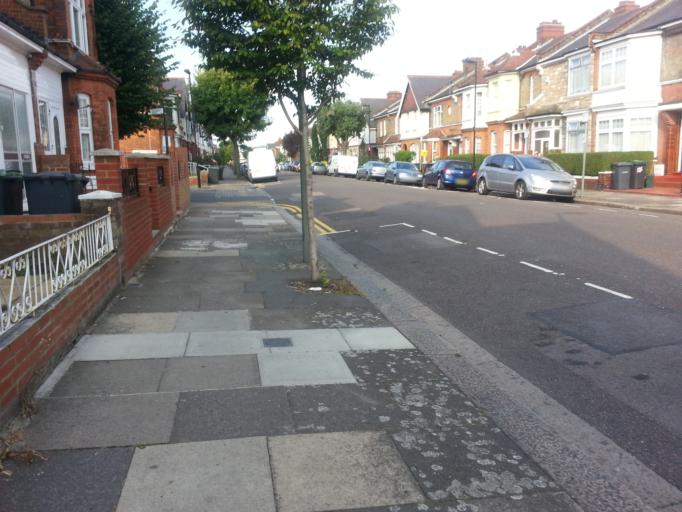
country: GB
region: England
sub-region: Greater London
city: Harringay
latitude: 51.5951
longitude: -0.1009
